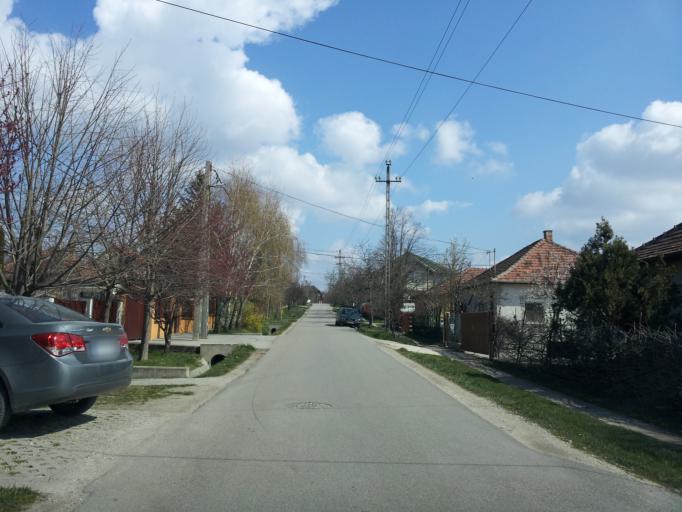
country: HU
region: Pest
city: Erd
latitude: 47.3923
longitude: 18.9191
